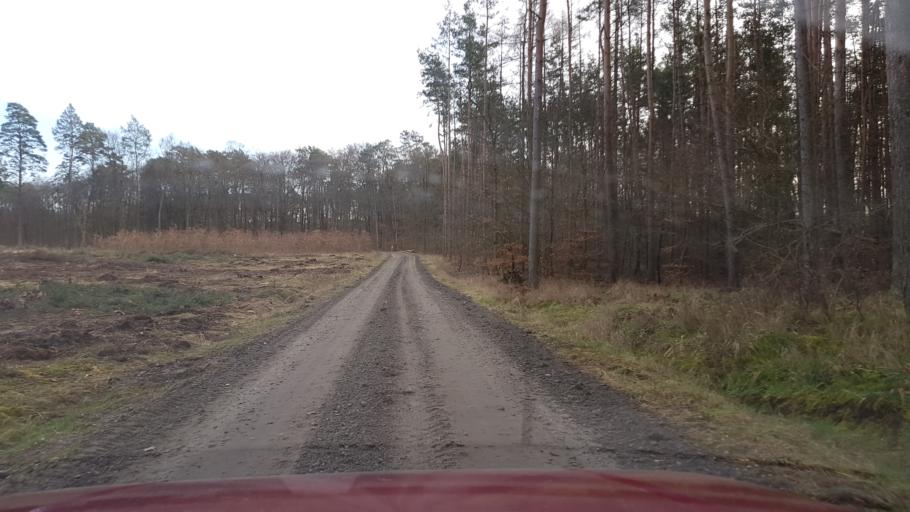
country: PL
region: Lubusz
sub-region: Powiat strzelecko-drezdenecki
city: Strzelce Krajenskie
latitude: 52.9113
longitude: 15.3817
